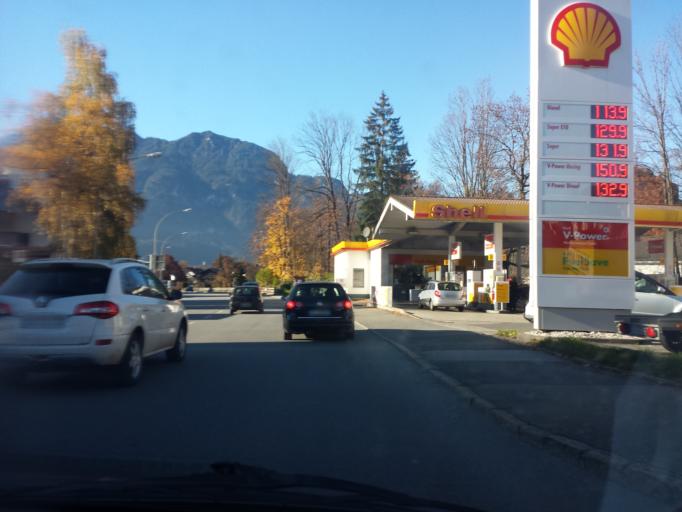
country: DE
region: Bavaria
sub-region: Upper Bavaria
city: Garmisch-Partenkirchen
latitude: 47.4898
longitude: 11.1131
